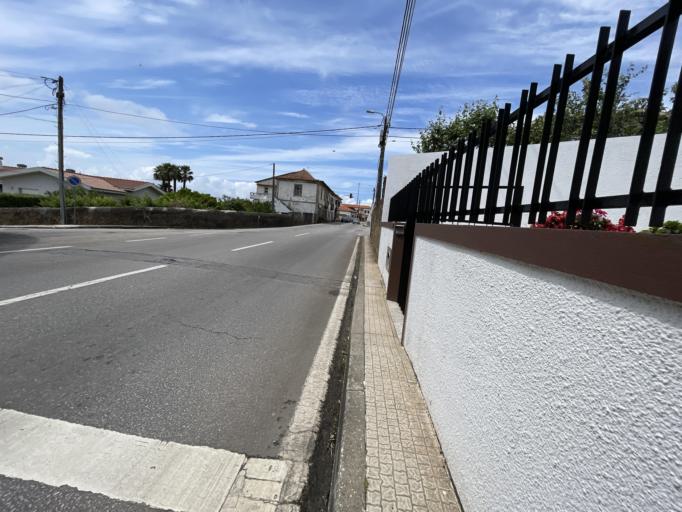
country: PT
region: Aveiro
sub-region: Ovar
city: Cortegaca
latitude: 40.9431
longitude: -8.6210
